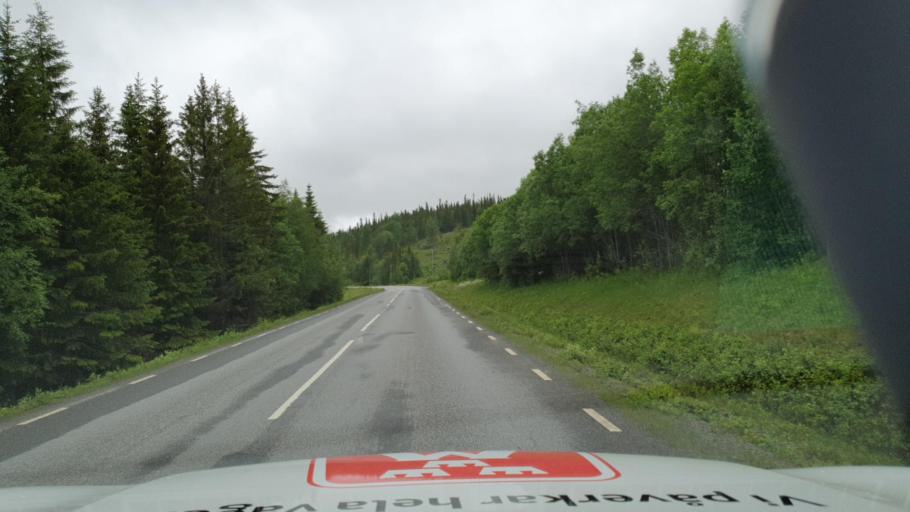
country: SE
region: Jaemtland
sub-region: Are Kommun
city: Are
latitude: 63.5473
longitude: 13.0403
